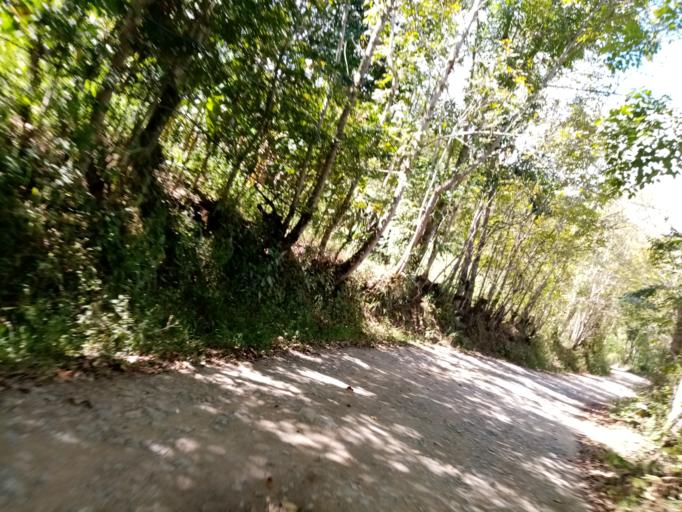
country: CO
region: Cundinamarca
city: Tenza
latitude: 5.0764
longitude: -73.4309
